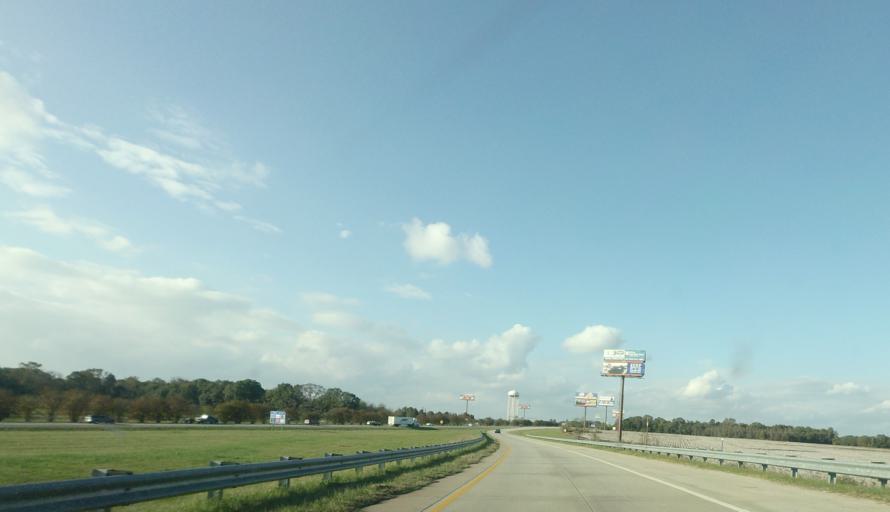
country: US
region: Georgia
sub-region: Houston County
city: Centerville
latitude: 32.5881
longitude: -83.7417
